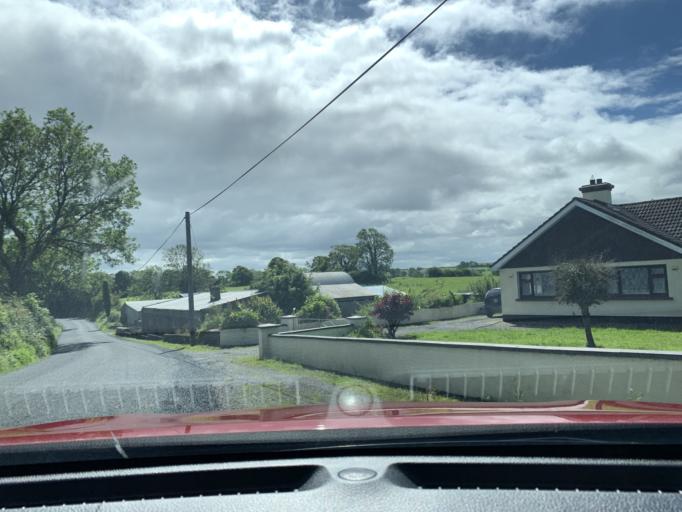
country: IE
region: Connaught
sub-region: County Leitrim
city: Carrick-on-Shannon
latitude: 53.8505
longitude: -8.1490
